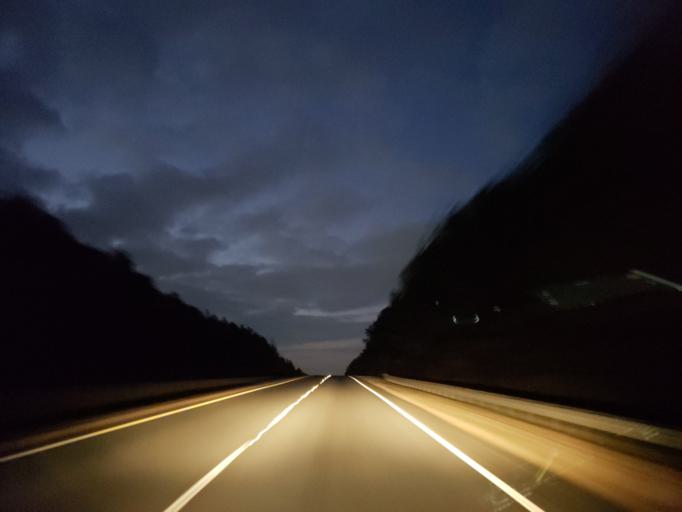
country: US
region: Georgia
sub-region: Polk County
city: Rockmart
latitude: 33.9779
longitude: -85.0084
